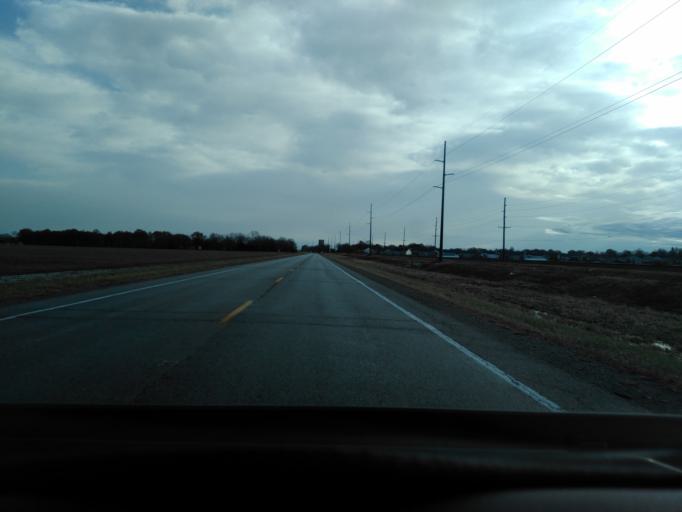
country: US
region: Illinois
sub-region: Madison County
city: Saint Jacob
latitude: 38.7180
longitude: -89.7835
